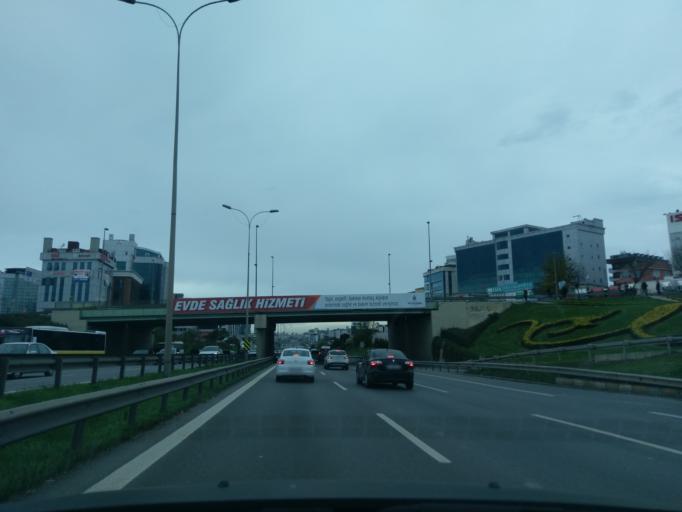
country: TR
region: Istanbul
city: Maltepe
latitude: 40.9302
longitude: 29.1458
